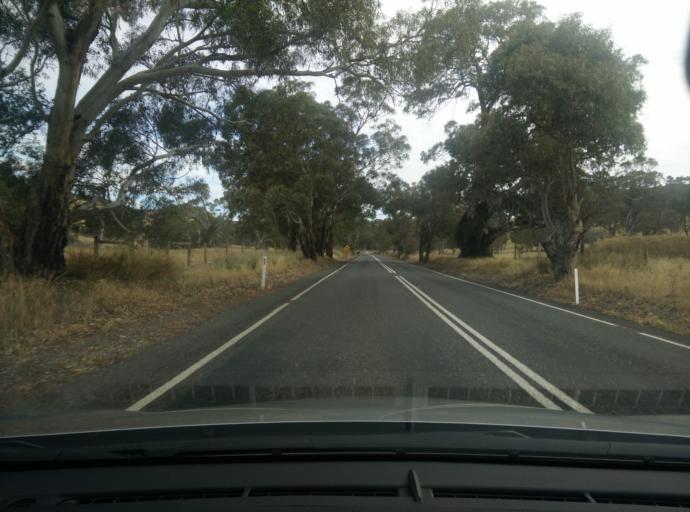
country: AU
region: South Australia
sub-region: Yankalilla
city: Normanville
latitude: -35.4863
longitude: 138.2786
